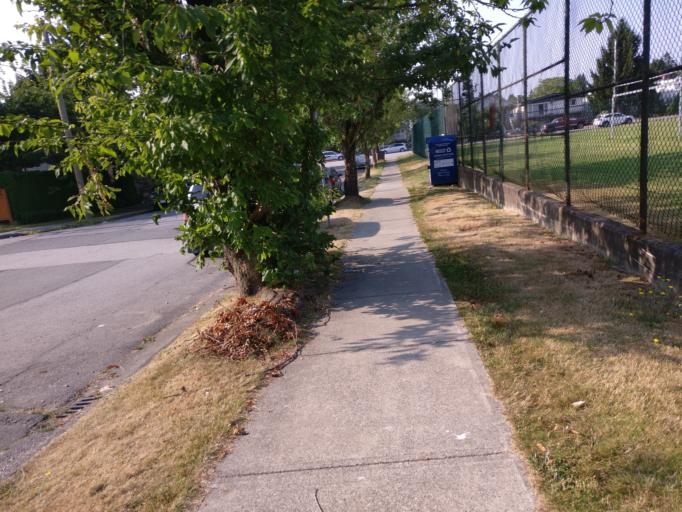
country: CA
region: British Columbia
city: Vancouver
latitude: 49.2494
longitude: -123.0921
